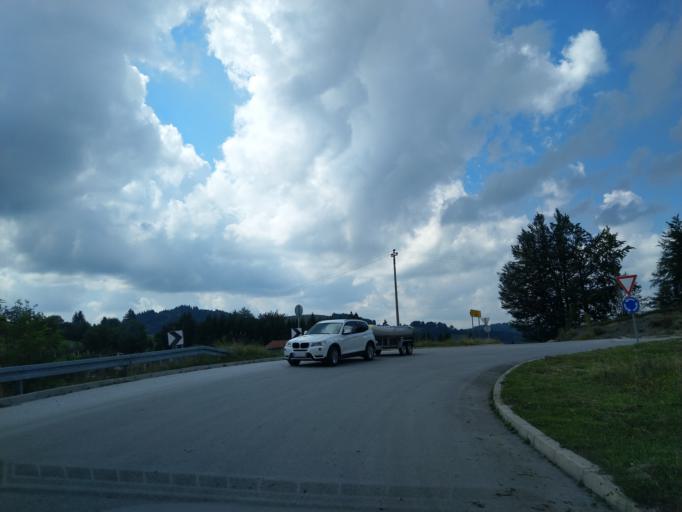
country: RS
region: Central Serbia
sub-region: Zlatiborski Okrug
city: Nova Varos
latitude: 43.5572
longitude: 19.8995
